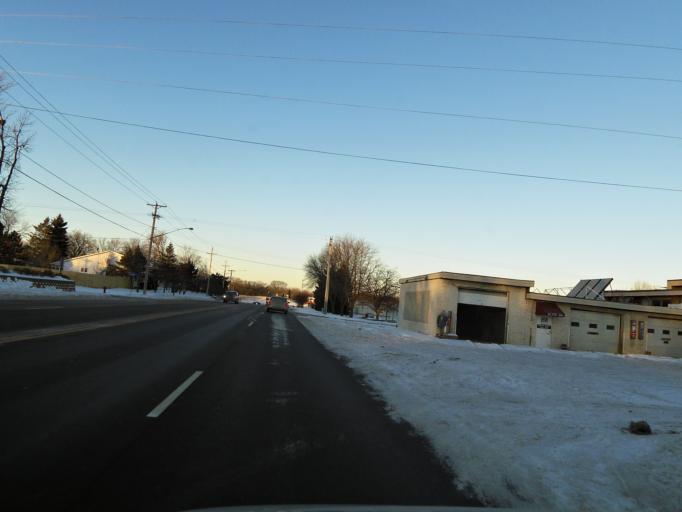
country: US
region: Minnesota
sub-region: Scott County
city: Prior Lake
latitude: 44.7174
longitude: -93.4169
